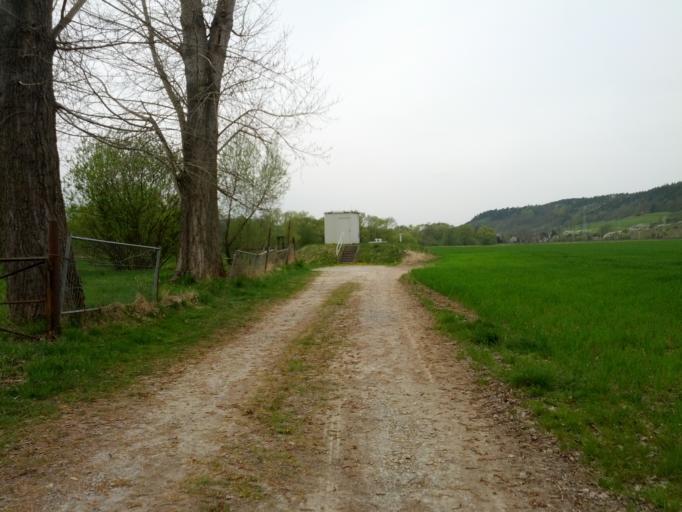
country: DE
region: Thuringia
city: Thal
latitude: 50.9598
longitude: 10.3813
